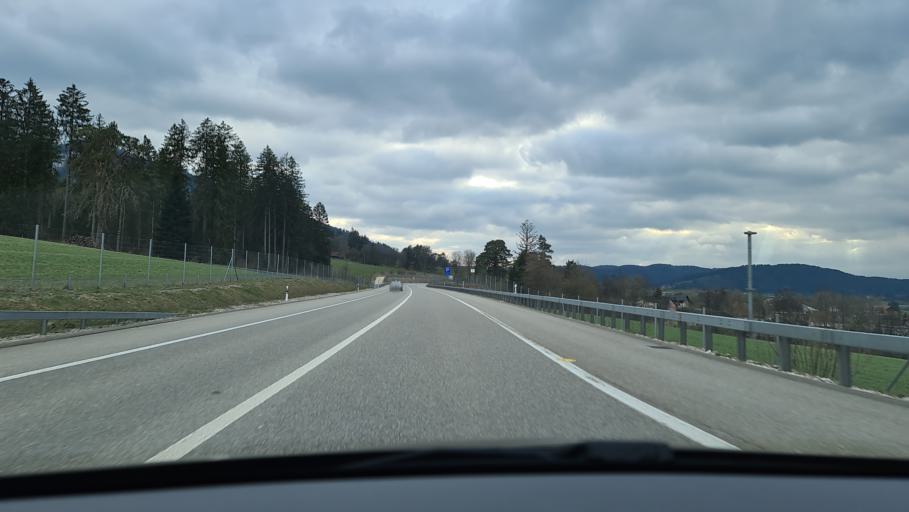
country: CH
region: Bern
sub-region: Jura bernois
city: Reconvilier
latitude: 47.2311
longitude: 7.2339
